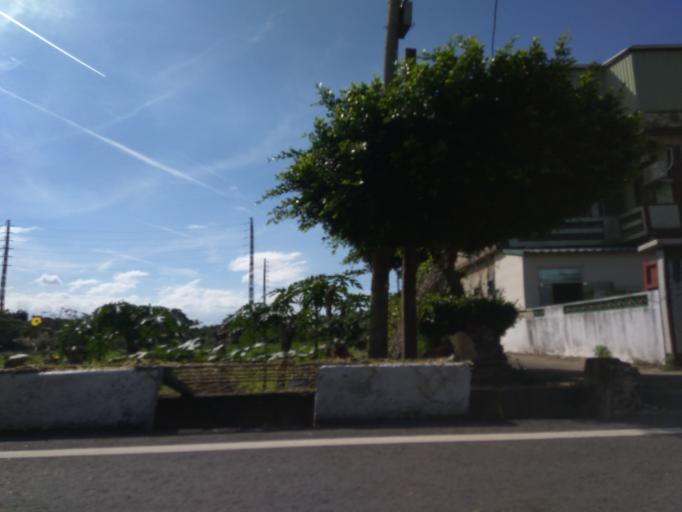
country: TW
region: Taiwan
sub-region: Hsinchu
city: Zhubei
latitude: 24.9934
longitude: 121.0466
